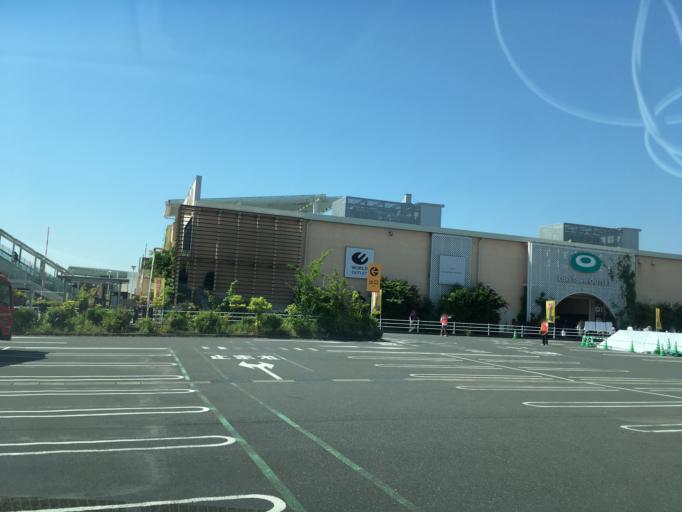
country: JP
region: Saitama
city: Yoshikawa
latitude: 35.8819
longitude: 139.8259
